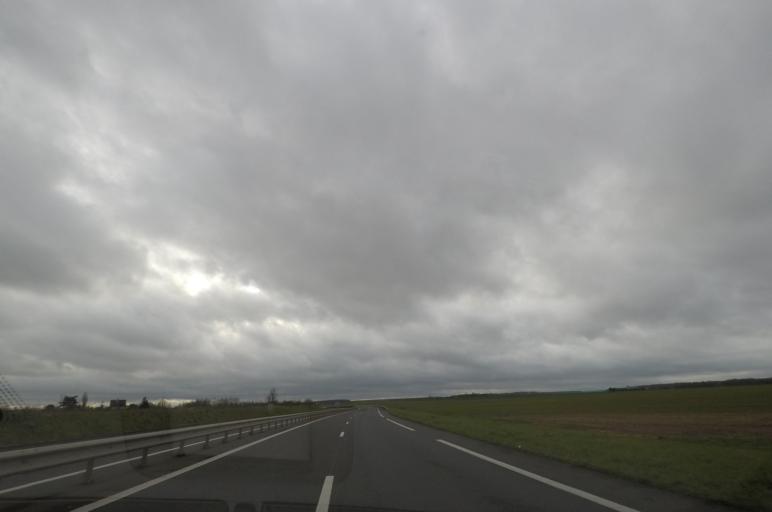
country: FR
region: Centre
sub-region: Departement du Loir-et-Cher
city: Saint-Sulpice-de-Pommeray
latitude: 47.6721
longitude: 1.2318
